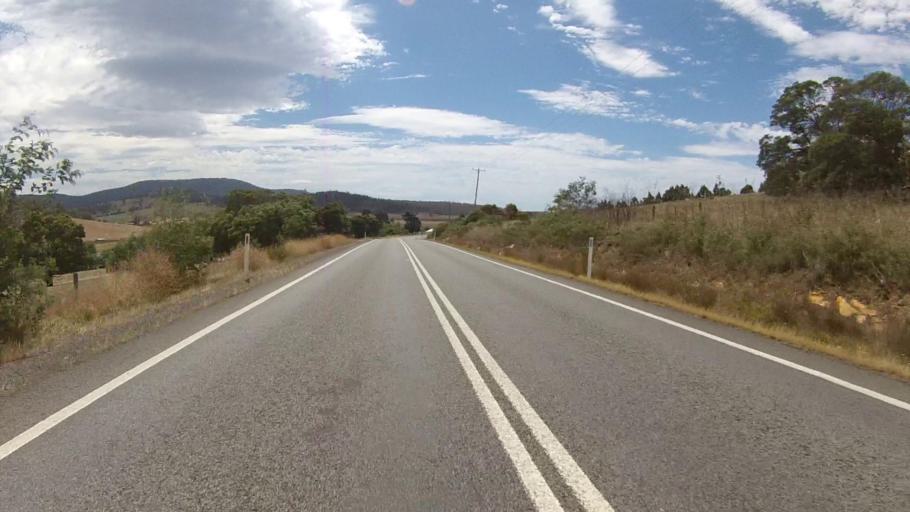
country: AU
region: Tasmania
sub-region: Brighton
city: Old Beach
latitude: -42.6693
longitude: 147.3692
